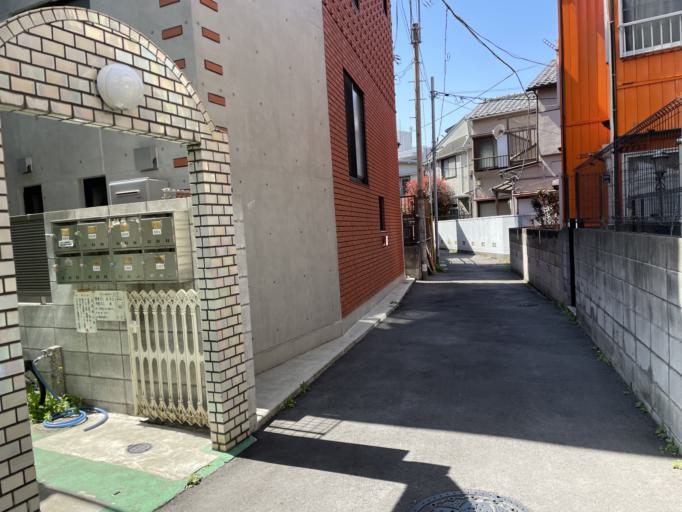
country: JP
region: Tokyo
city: Tokyo
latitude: 35.7071
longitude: 139.6683
